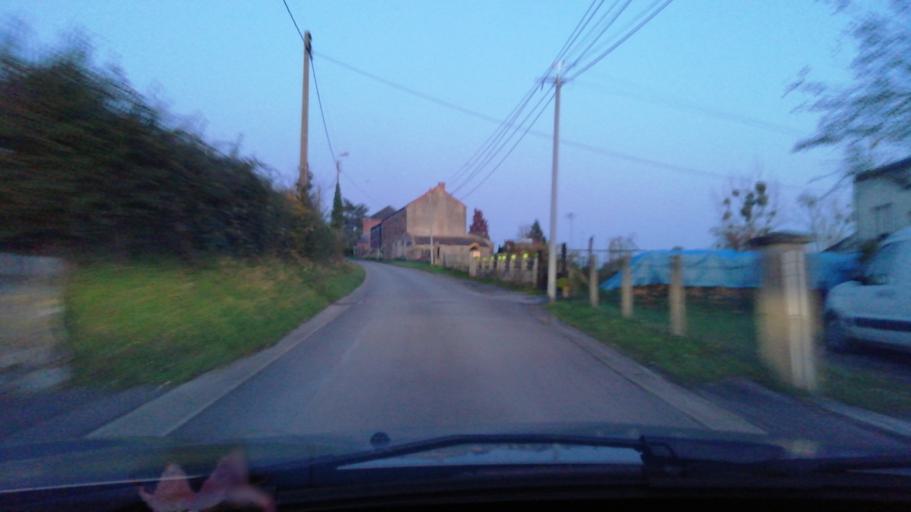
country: FR
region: Nord-Pas-de-Calais
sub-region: Departement du Nord
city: Marpent
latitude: 50.2569
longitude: 4.0812
